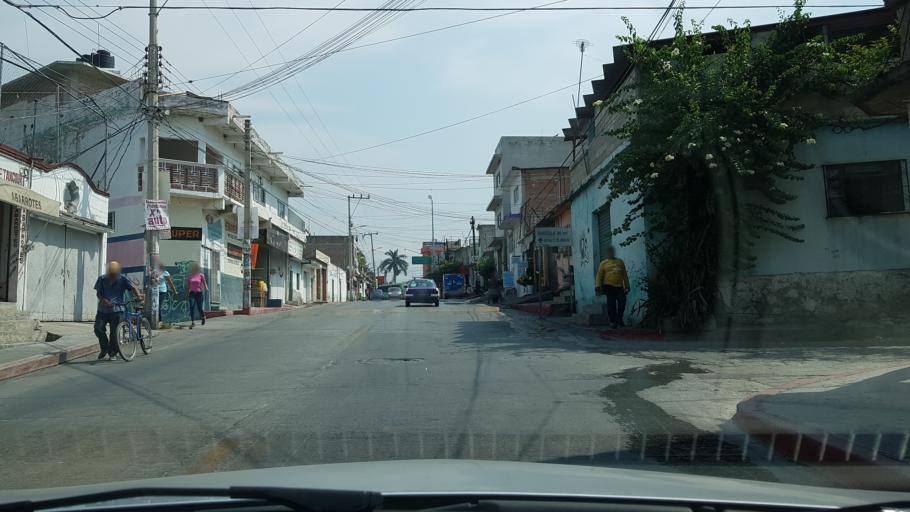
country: MX
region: Morelos
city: Emiliano Zapata
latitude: 18.8364
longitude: -99.1835
